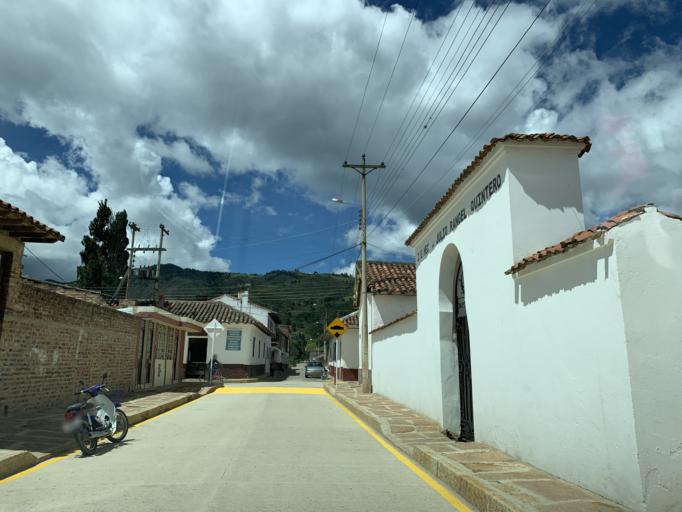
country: CO
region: Boyaca
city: Floresta
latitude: 5.8589
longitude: -72.9182
